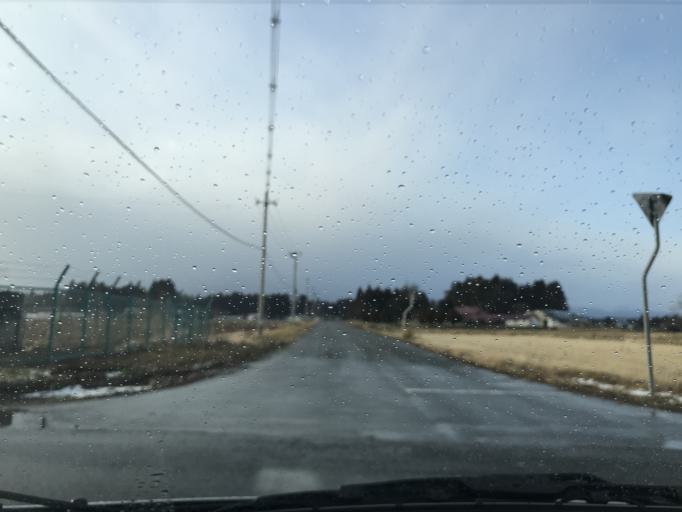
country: JP
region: Iwate
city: Mizusawa
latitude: 39.0960
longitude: 141.0235
